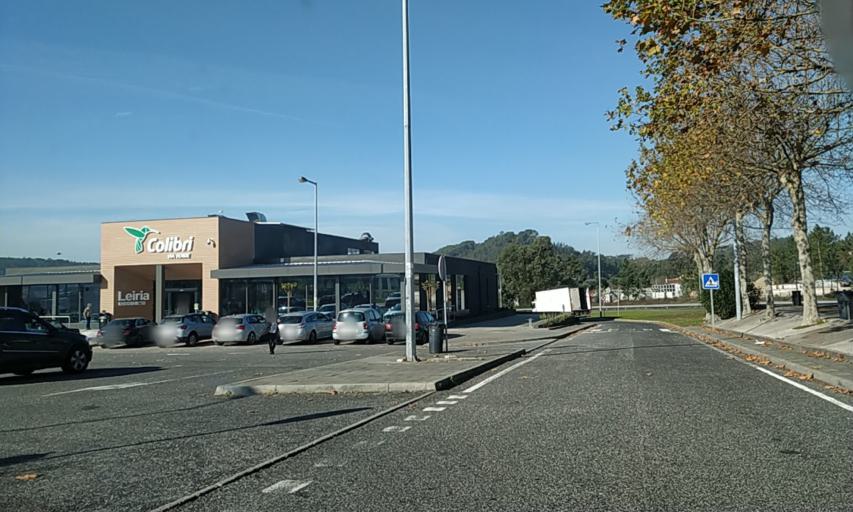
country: PT
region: Leiria
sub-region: Leiria
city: Caranguejeira
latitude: 39.7134
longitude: -8.7097
